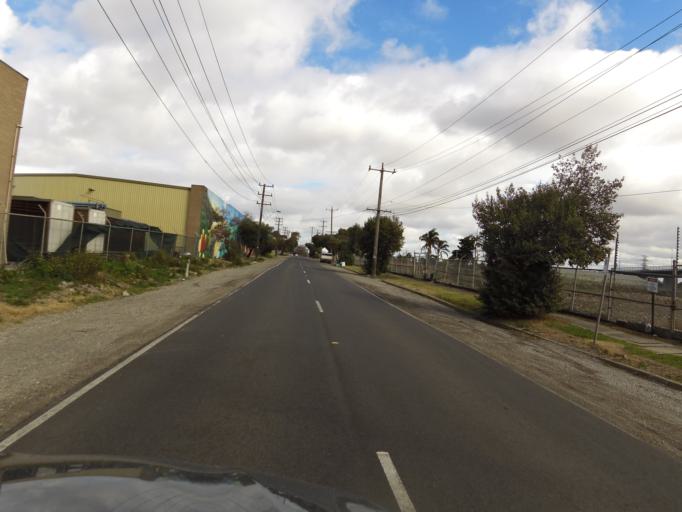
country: AU
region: Victoria
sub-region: Hobsons Bay
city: Spotswood
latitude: -37.8284
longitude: 144.8921
